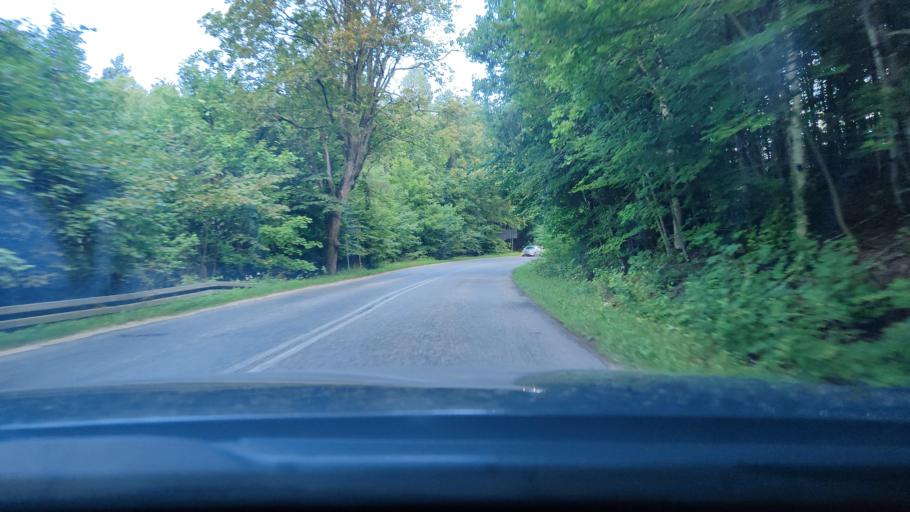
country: PL
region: Pomeranian Voivodeship
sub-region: Powiat wejherowski
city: Orle
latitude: 54.7077
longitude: 18.1598
